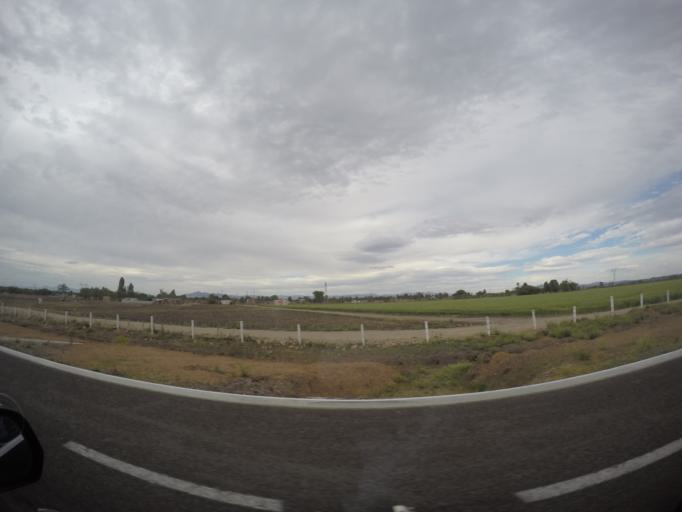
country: MX
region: Guanajuato
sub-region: Irapuato
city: Serrano
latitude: 20.8044
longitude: -101.4323
